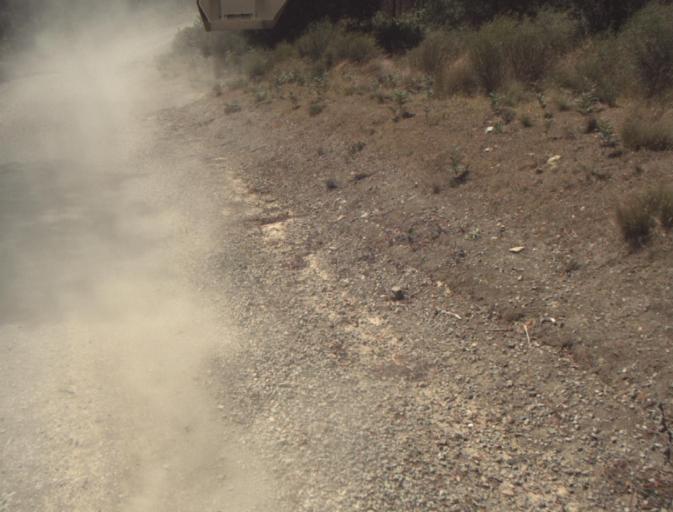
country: AU
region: Tasmania
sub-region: Dorset
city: Scottsdale
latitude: -41.3098
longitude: 147.4655
